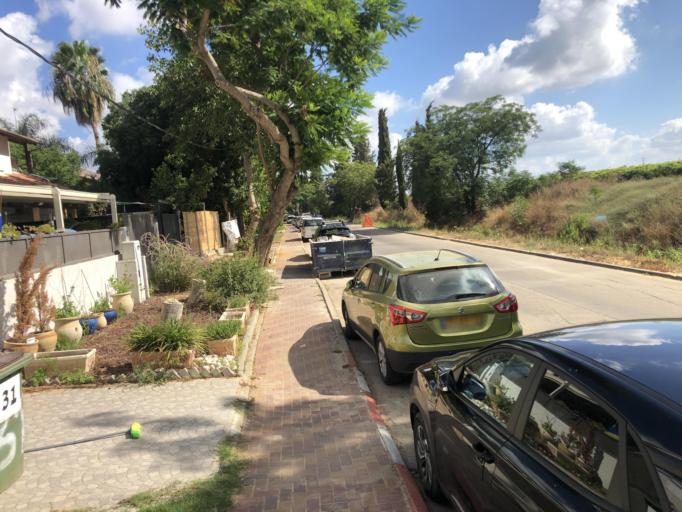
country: IL
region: Central District
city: Yehud
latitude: 32.0358
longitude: 34.8988
